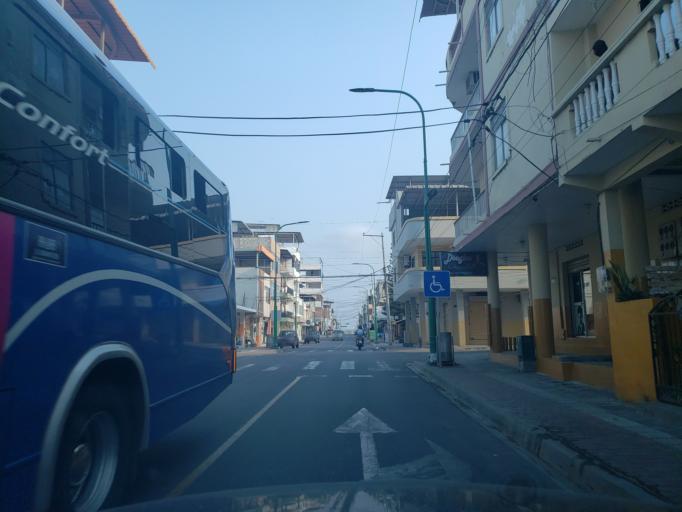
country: EC
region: Manabi
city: Manta
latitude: -0.9522
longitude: -80.7293
